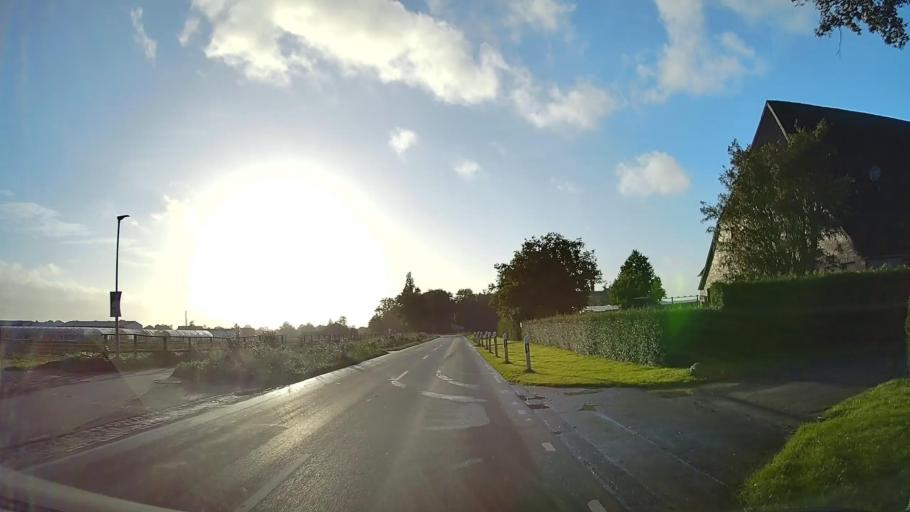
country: DE
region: Schleswig-Holstein
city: Herzhorn
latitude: 53.7893
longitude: 9.4575
